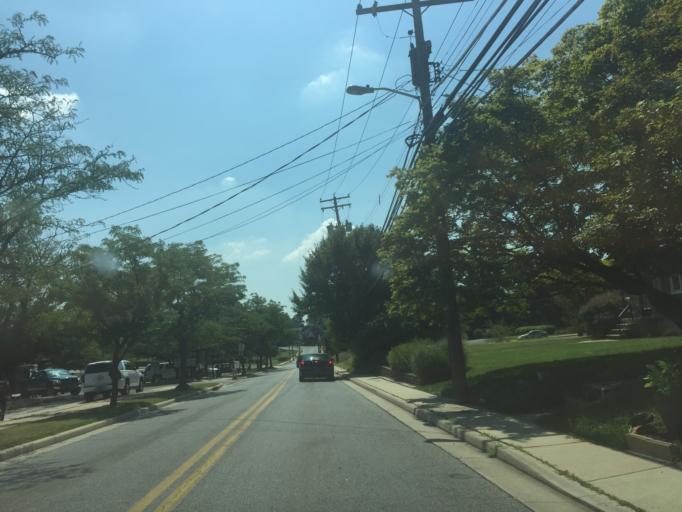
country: US
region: Maryland
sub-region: Baltimore County
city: Overlea
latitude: 39.3603
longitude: -76.5206
